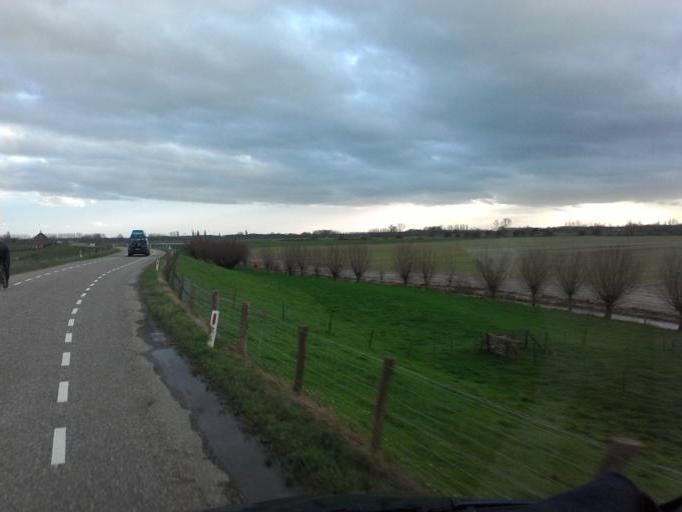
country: NL
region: Gelderland
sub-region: Gemeente Culemborg
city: Culemborg
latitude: 51.9715
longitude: 5.2681
